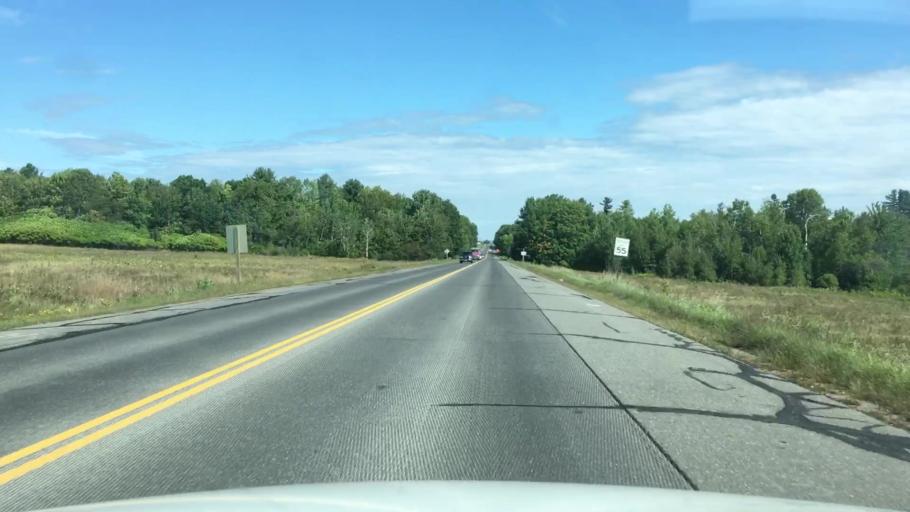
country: US
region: Maine
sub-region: Penobscot County
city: Newport
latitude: 44.8639
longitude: -69.2842
